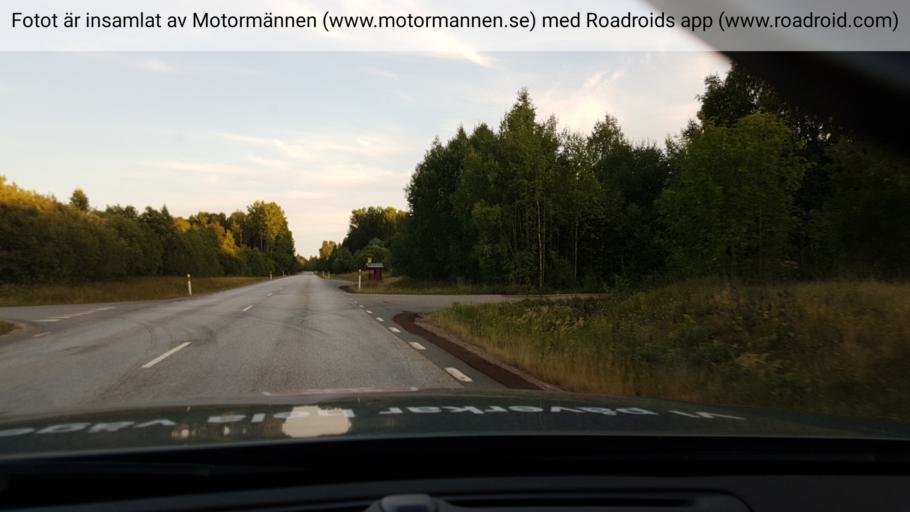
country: SE
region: Vaermland
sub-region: Storfors Kommun
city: Storfors
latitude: 59.5304
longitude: 14.2954
